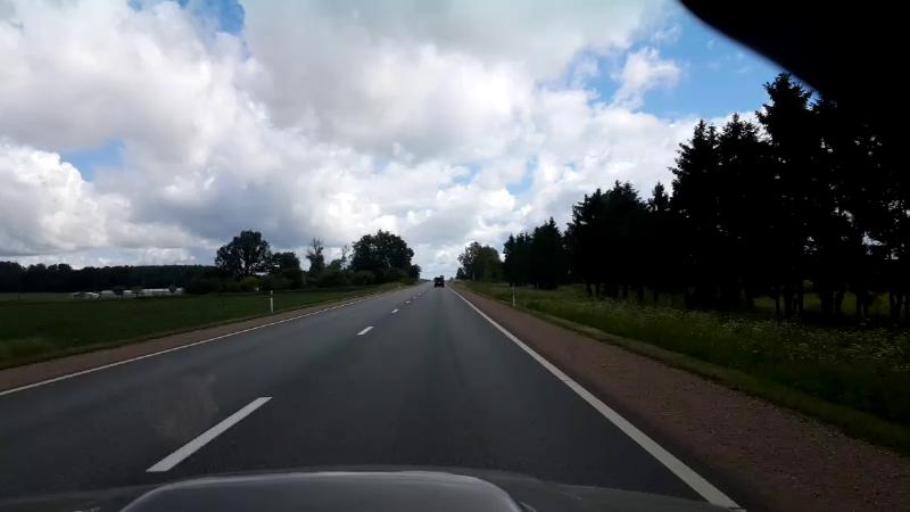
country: LV
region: Bauskas Rajons
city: Bauska
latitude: 56.4759
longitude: 24.1710
